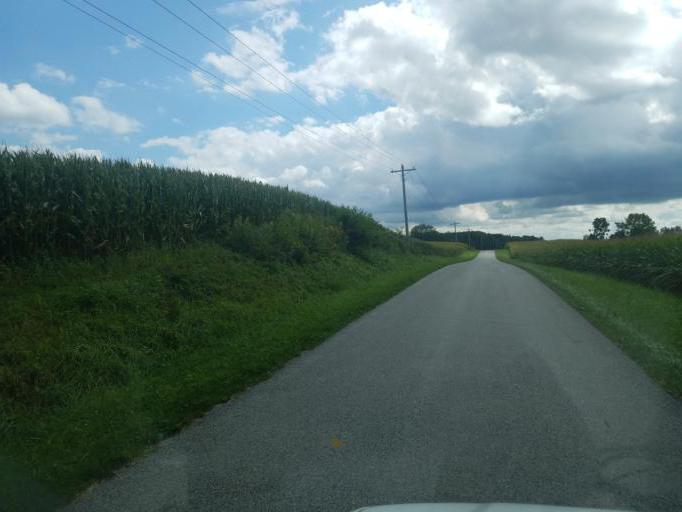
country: US
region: Ohio
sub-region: Huron County
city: Willard
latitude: 41.0934
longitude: -82.6312
